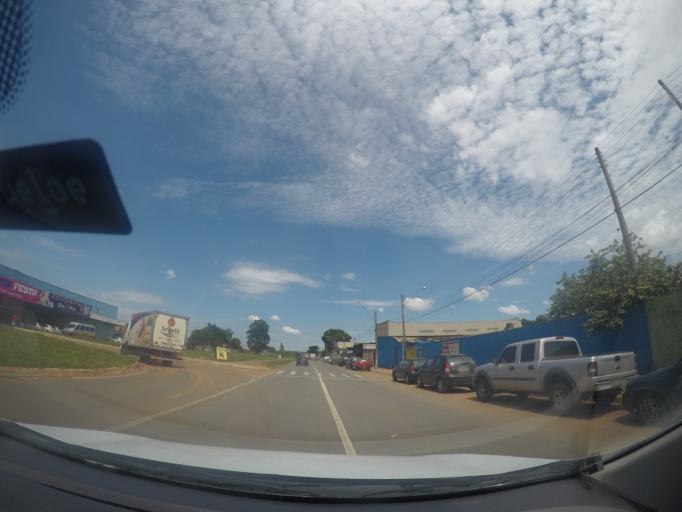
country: BR
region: Goias
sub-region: Goiania
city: Goiania
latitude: -16.6814
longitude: -49.3288
